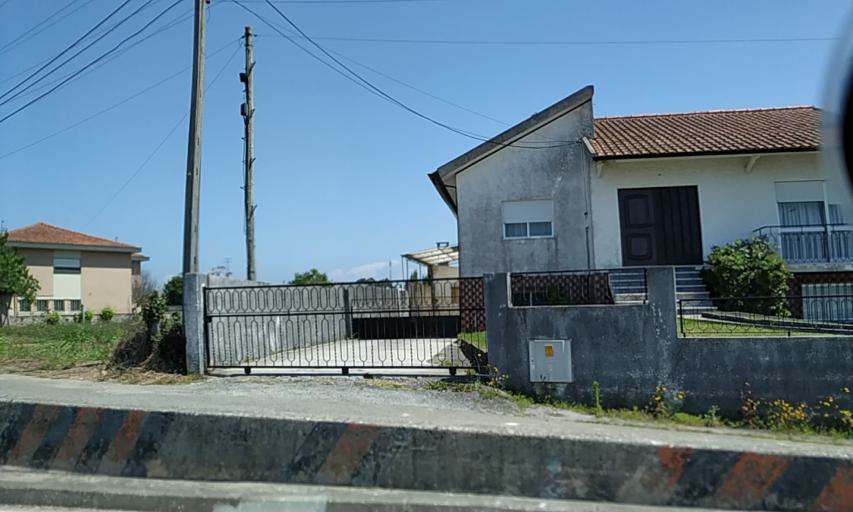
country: PT
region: Aveiro
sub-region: Aveiro
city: Aveiro
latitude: 40.6467
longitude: -8.6259
